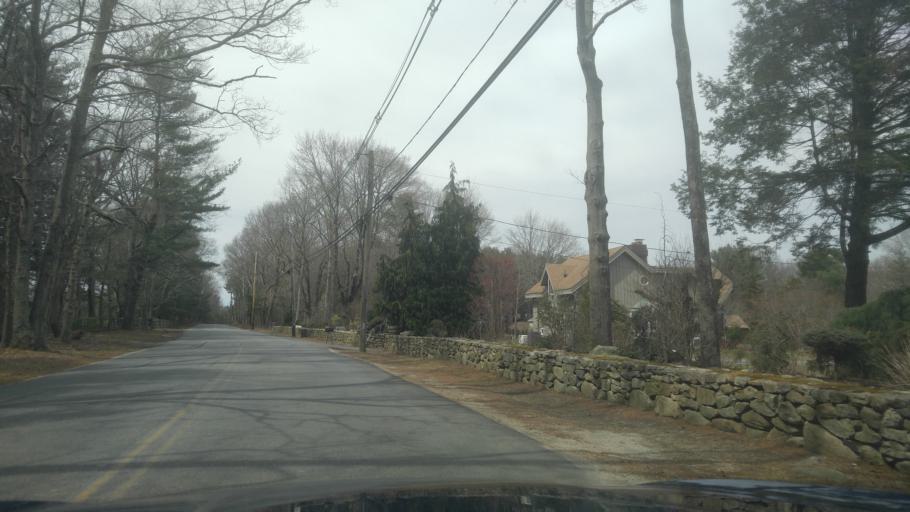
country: US
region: Rhode Island
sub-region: Washington County
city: Exeter
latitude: 41.6254
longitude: -71.5671
